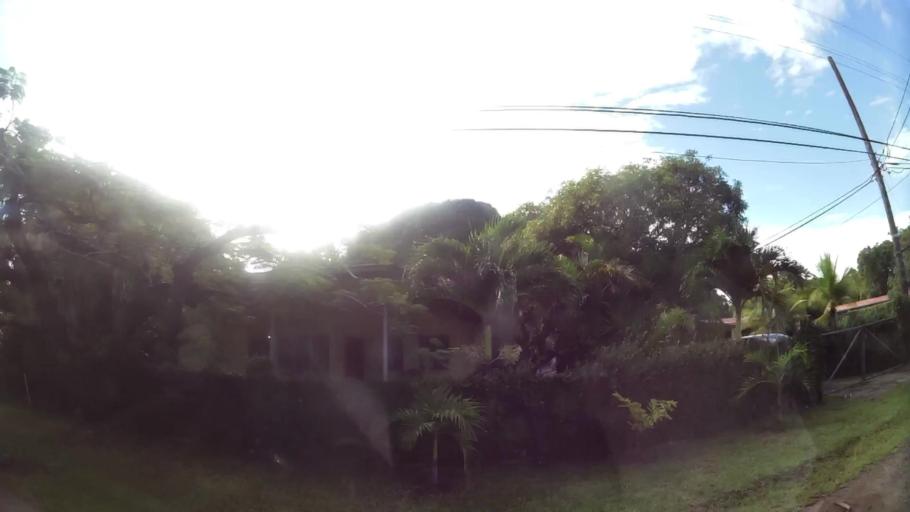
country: PA
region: Panama
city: Nueva Gorgona
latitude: 8.5309
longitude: -79.8811
